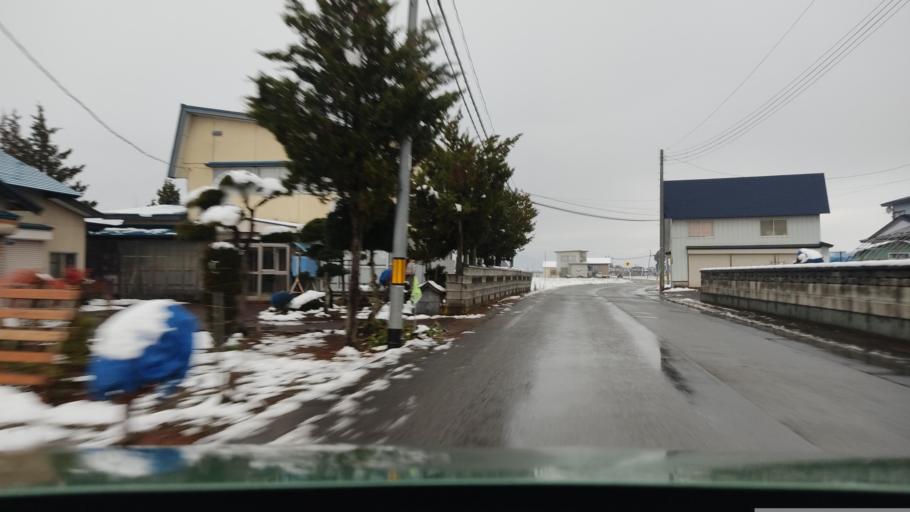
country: JP
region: Akita
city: Omagari
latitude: 39.4660
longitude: 140.5280
